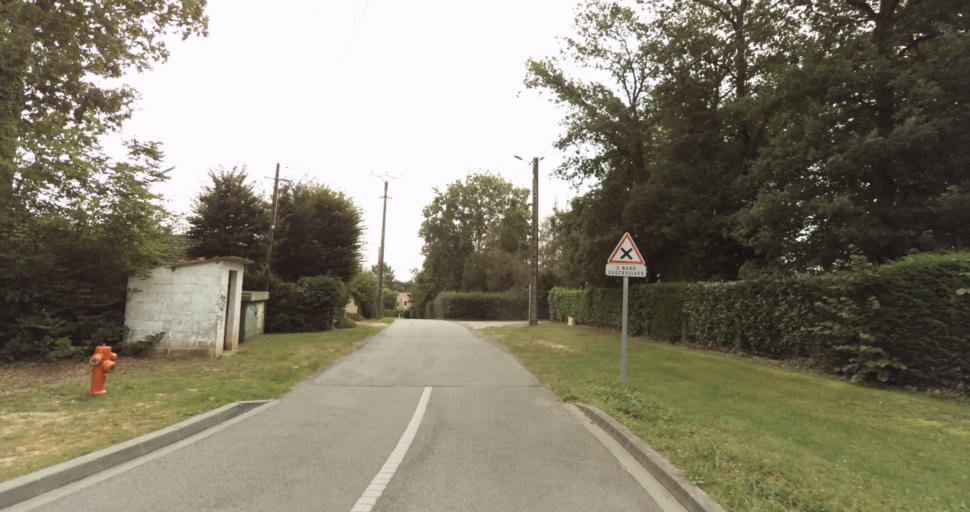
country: FR
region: Haute-Normandie
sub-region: Departement de l'Eure
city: Croth
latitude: 48.8698
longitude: 1.3605
